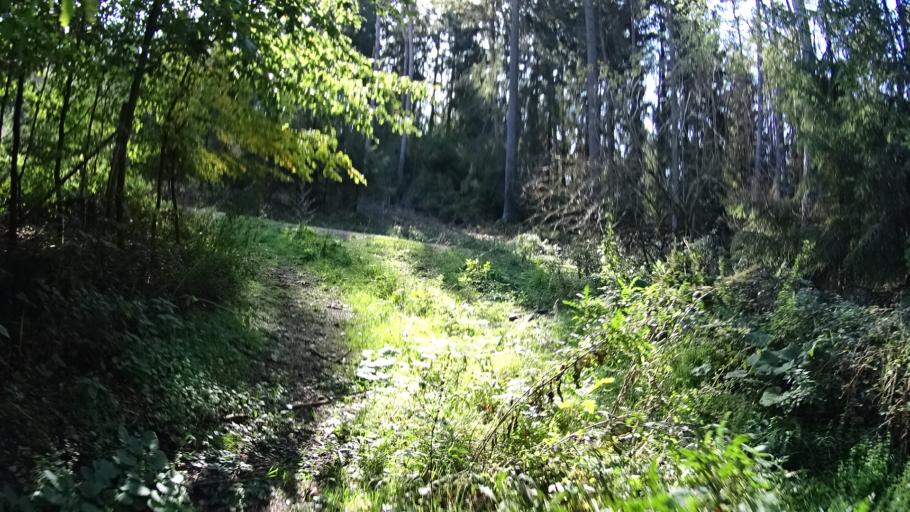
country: DE
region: Bavaria
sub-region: Upper Bavaria
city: Hitzhofen
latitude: 48.8493
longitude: 11.3443
